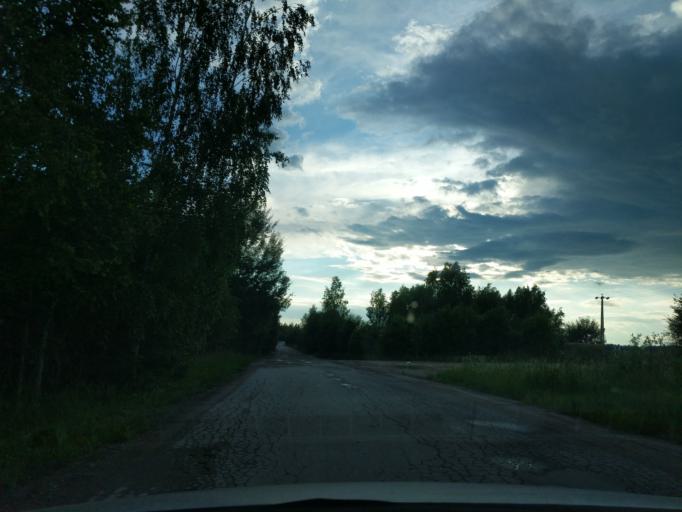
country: RU
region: Kaluga
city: Myatlevo
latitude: 54.8531
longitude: 35.5919
